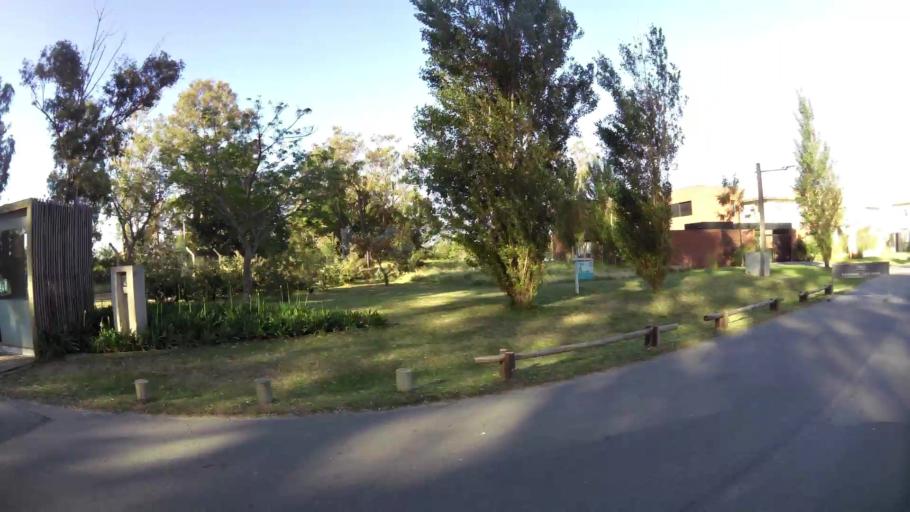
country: UY
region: Canelones
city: Paso de Carrasco
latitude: -34.8649
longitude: -56.0445
